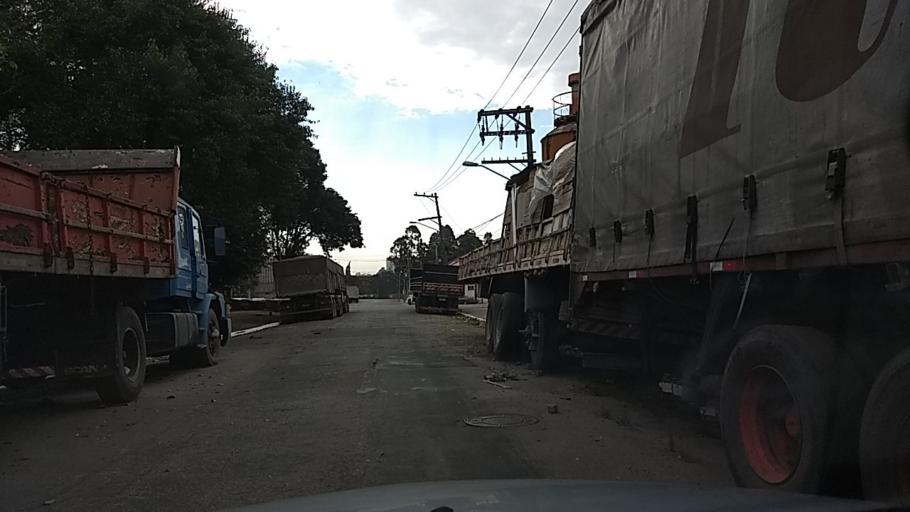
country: BR
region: Sao Paulo
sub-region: Guarulhos
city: Guarulhos
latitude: -23.4963
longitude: -46.5679
